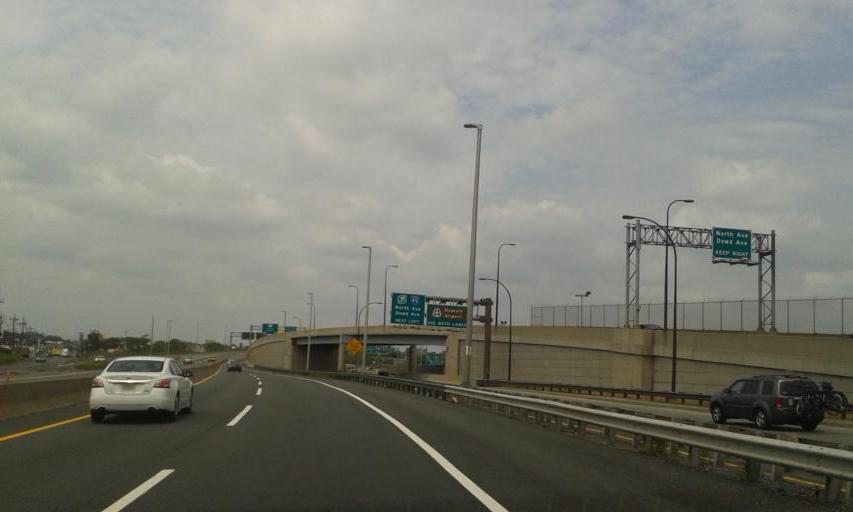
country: US
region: New Jersey
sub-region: Union County
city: Elizabeth
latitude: 40.6733
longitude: -74.1867
